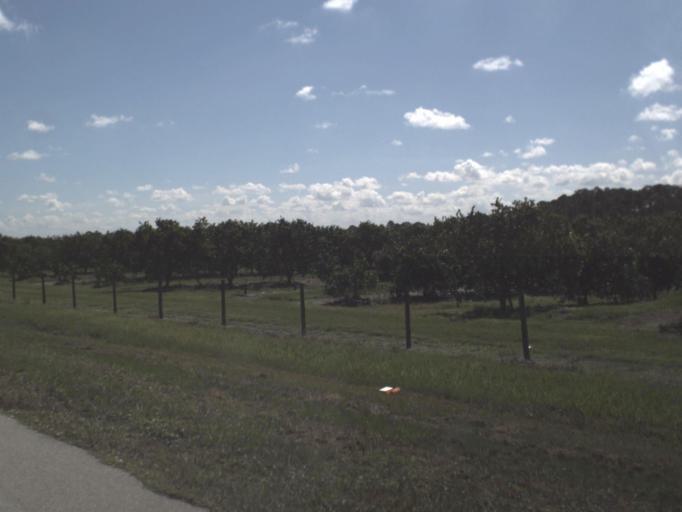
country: US
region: Florida
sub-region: Hendry County
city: Port LaBelle
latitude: 26.8121
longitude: -81.3955
